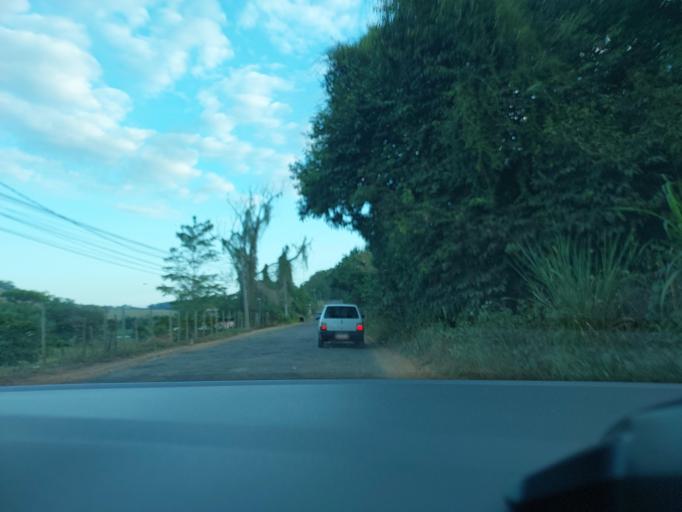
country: BR
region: Rio de Janeiro
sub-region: Natividade
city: Natividade
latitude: -21.1834
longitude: -42.1036
